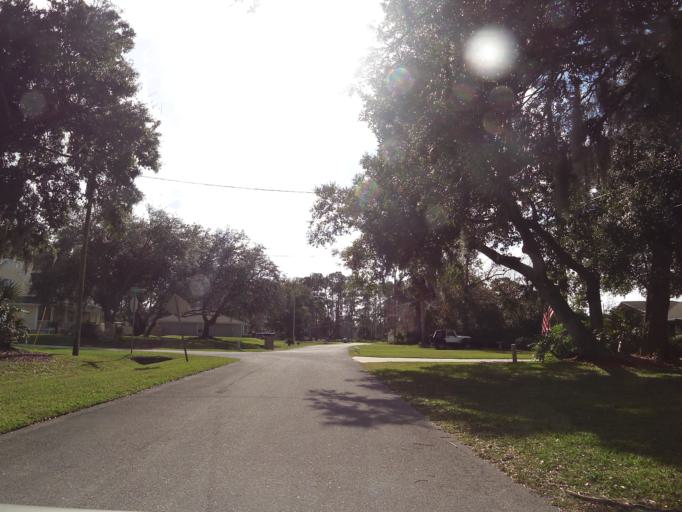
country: US
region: Florida
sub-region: Duval County
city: Atlantic Beach
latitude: 30.3607
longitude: -81.4638
